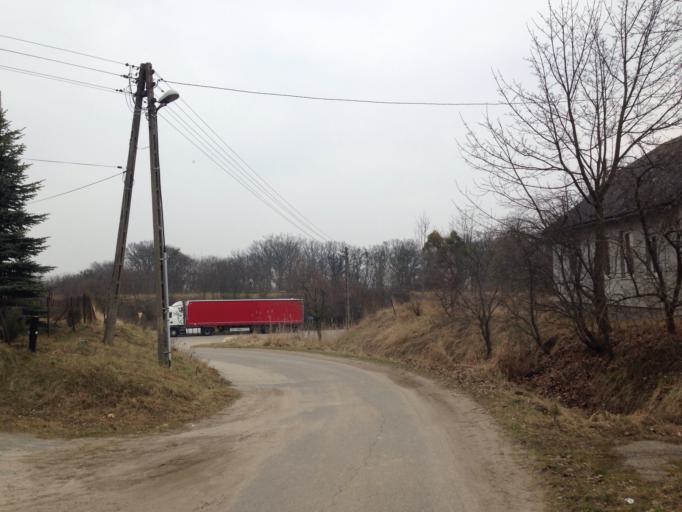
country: PL
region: Pomeranian Voivodeship
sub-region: Powiat kwidzynski
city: Sadlinki
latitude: 53.7328
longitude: 18.8253
